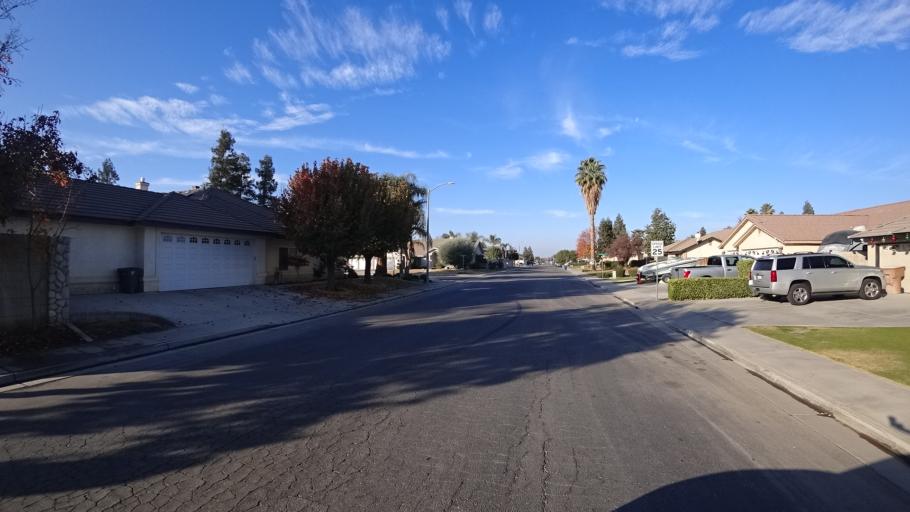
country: US
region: California
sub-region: Kern County
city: Greenfield
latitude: 35.2757
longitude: -119.0481
